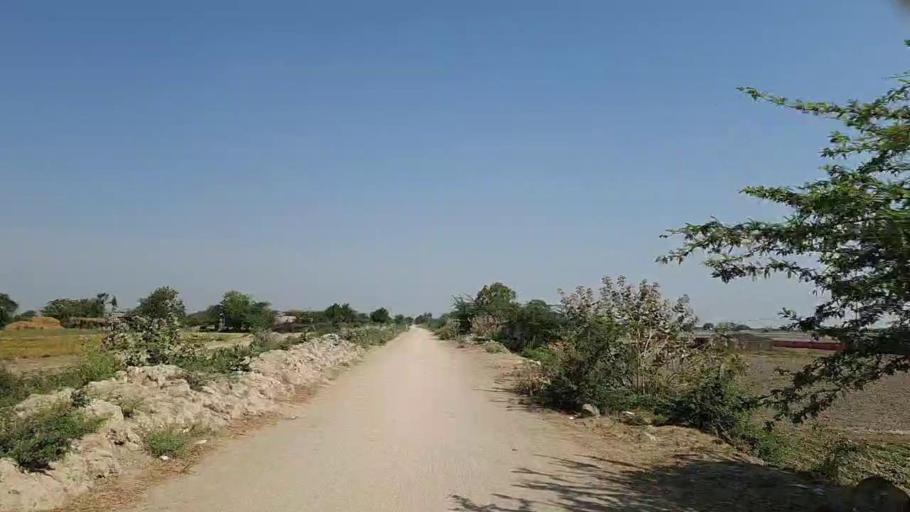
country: PK
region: Sindh
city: Mirpur Batoro
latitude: 24.6824
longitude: 68.2579
